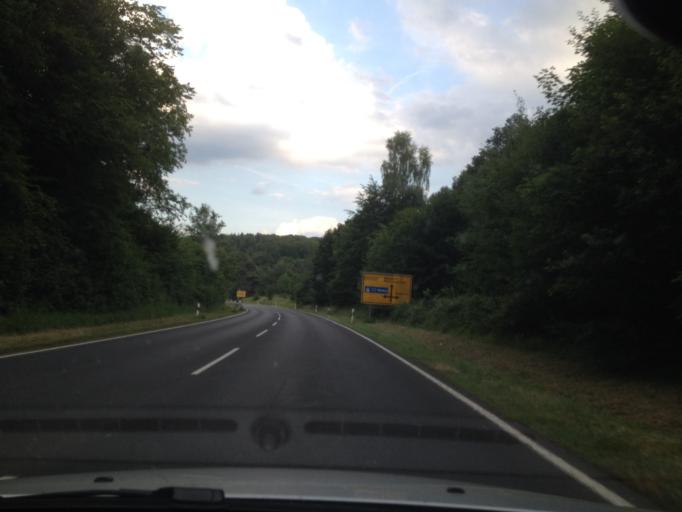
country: DE
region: Bavaria
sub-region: Regierungsbezirk Unterfranken
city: Weibersbrunn
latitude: 49.8952
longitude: 9.3931
